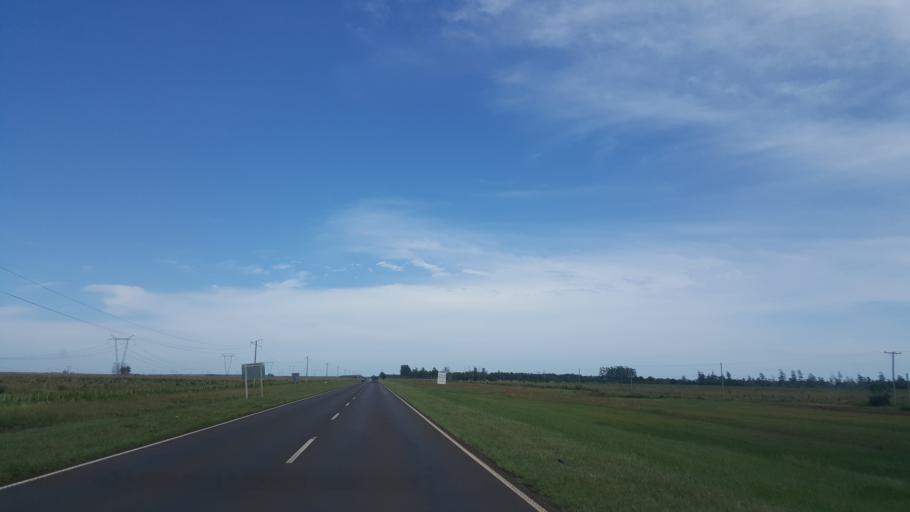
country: AR
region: Corrientes
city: Ituzaingo
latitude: -27.6054
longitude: -56.4460
